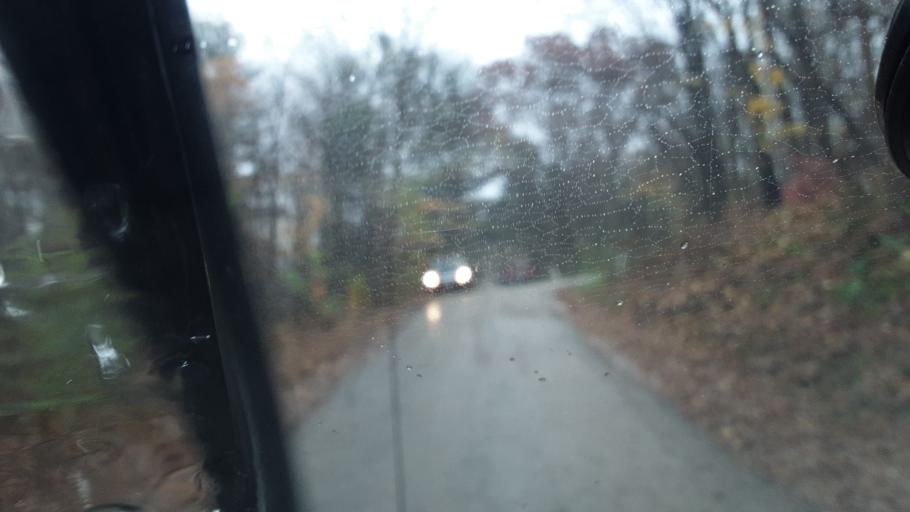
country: US
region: Ohio
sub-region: Vinton County
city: McArthur
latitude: 39.2250
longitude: -82.4609
